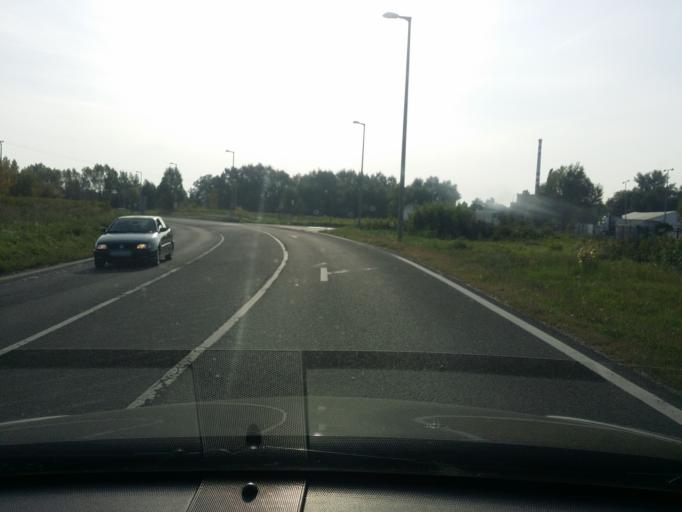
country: HU
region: Budapest
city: Budapest XV. keruelet
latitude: 47.5890
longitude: 19.1272
